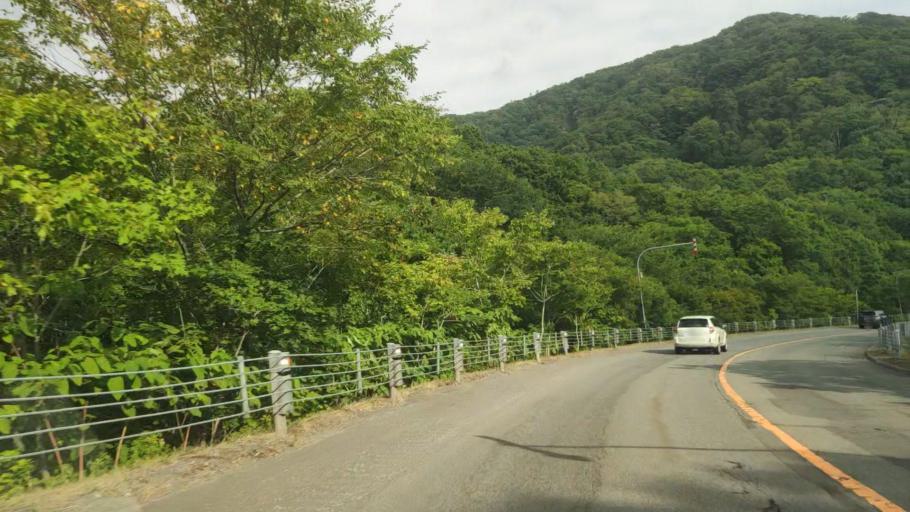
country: JP
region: Hokkaido
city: Ishikari
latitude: 43.4844
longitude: 141.4004
